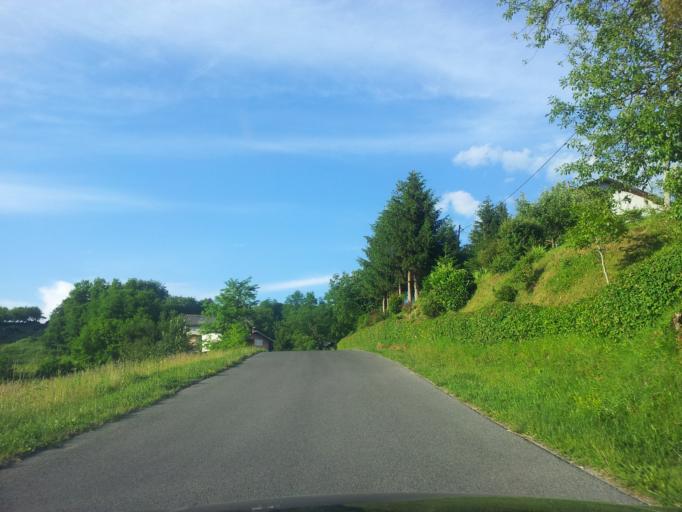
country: HR
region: Karlovacka
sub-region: Grad Karlovac
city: Karlovac
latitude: 45.4810
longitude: 15.4804
